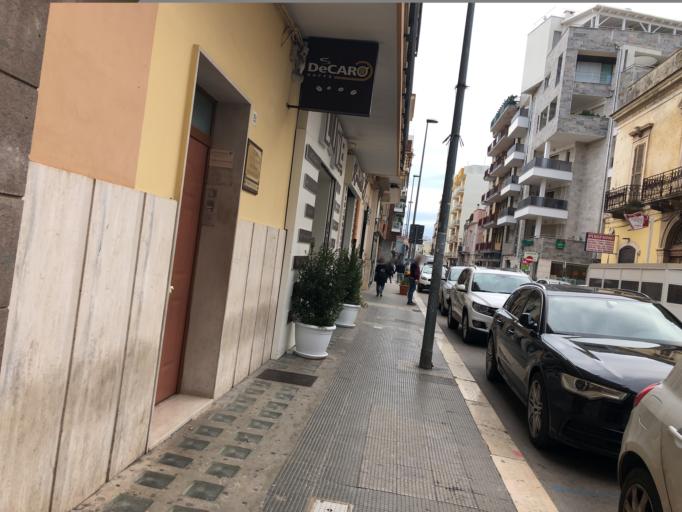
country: IT
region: Apulia
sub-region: Provincia di Bari
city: Bitonto
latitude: 41.1115
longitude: 16.6868
